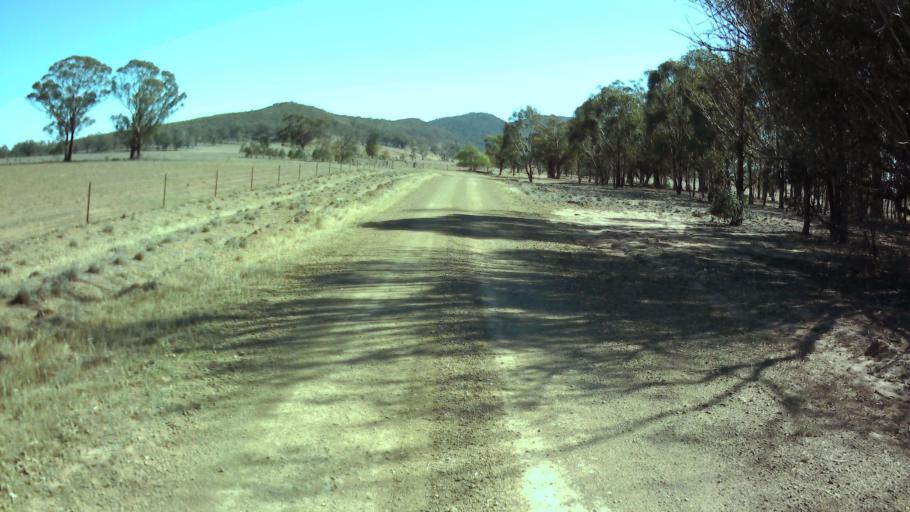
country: AU
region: New South Wales
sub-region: Weddin
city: Grenfell
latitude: -33.7648
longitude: 147.9237
